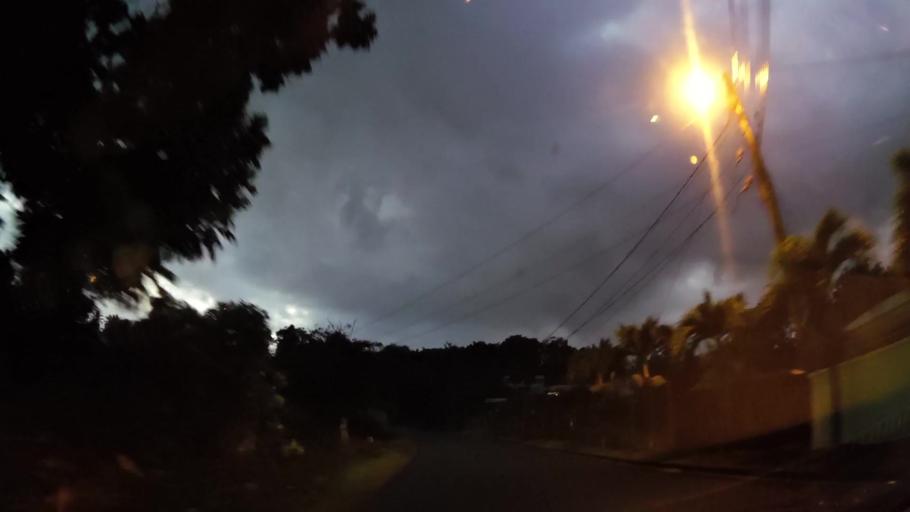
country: DM
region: Saint Andrew
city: Calibishie
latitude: 15.5908
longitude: -61.3402
